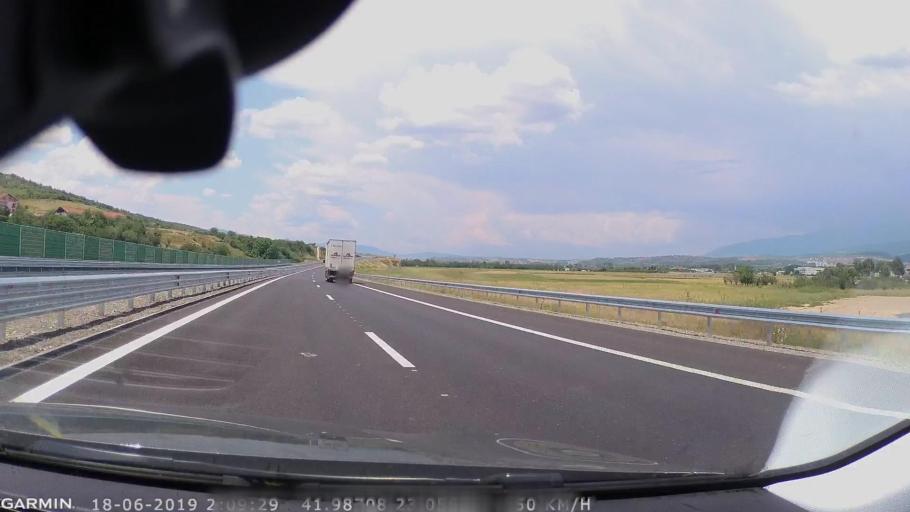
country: BG
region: Blagoevgrad
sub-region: Obshtina Blagoevgrad
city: Blagoevgrad
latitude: 41.9773
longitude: 23.0695
